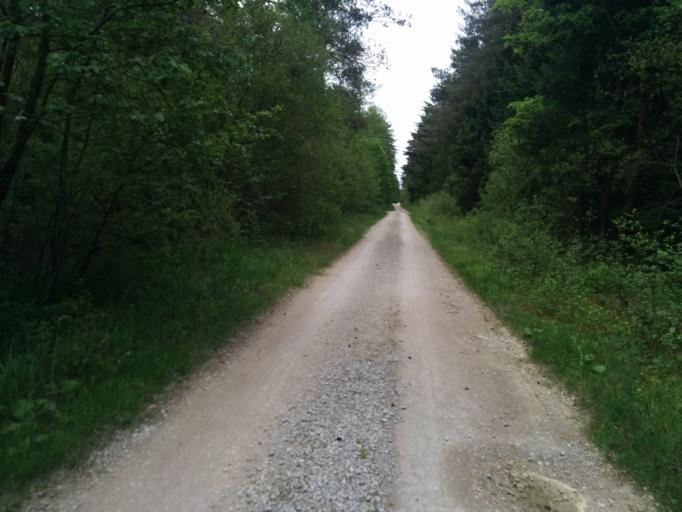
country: DE
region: Bavaria
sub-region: Regierungsbezirk Mittelfranken
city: Buckenhof
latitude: 49.5522
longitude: 11.0482
